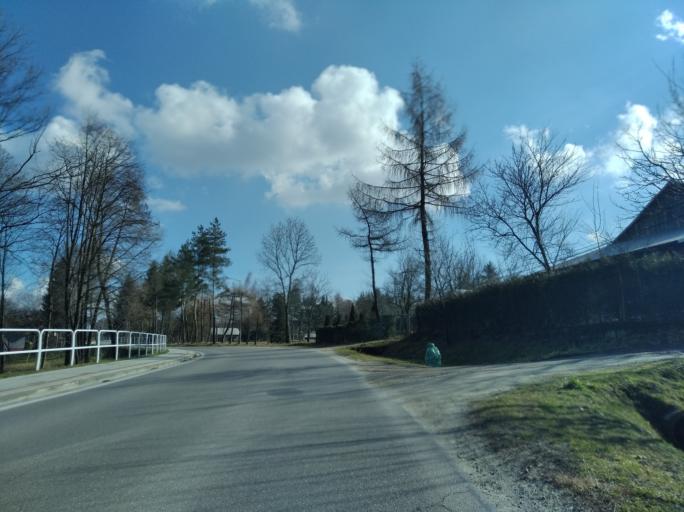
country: PL
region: Subcarpathian Voivodeship
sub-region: Powiat jasielski
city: Kolaczyce
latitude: 49.8509
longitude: 21.5164
